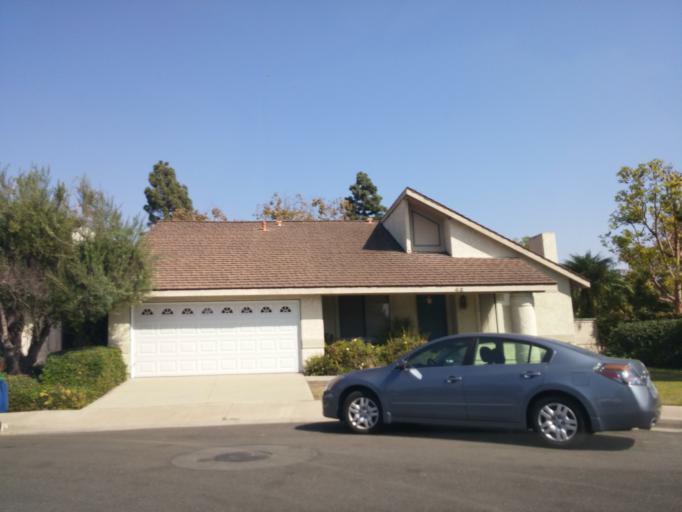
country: US
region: California
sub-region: Orange County
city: Irvine
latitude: 33.6907
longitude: -117.7876
